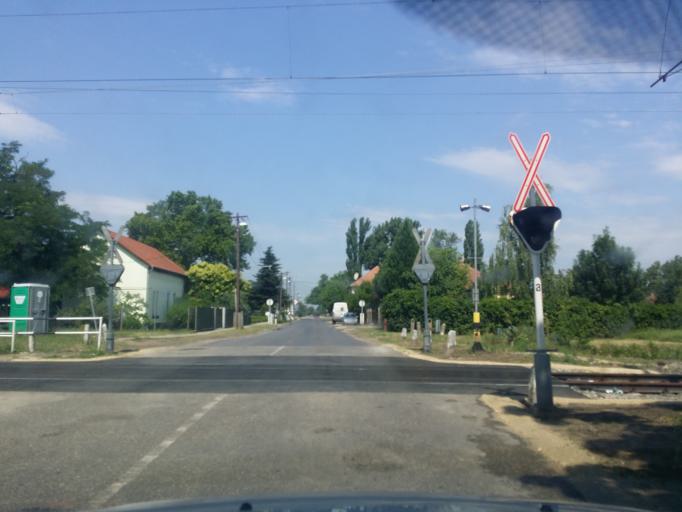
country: HU
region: Bacs-Kiskun
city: Jaszszentlaszlo
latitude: 46.5690
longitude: 19.7571
